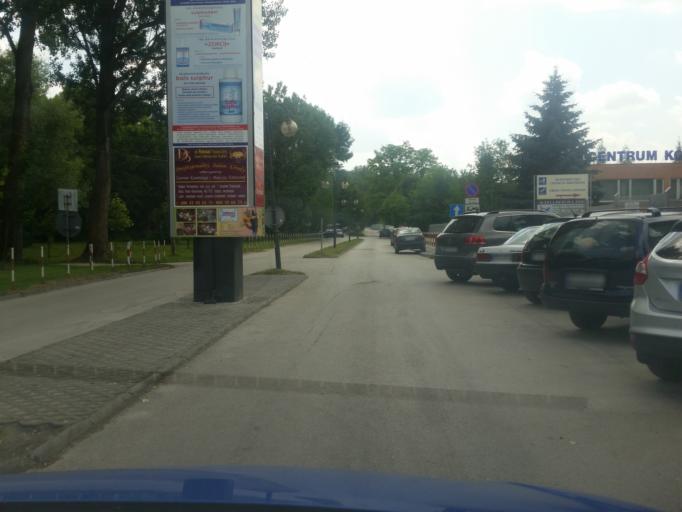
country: PL
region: Swietokrzyskie
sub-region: Powiat buski
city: Busko-Zdroj
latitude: 50.4558
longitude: 20.7174
